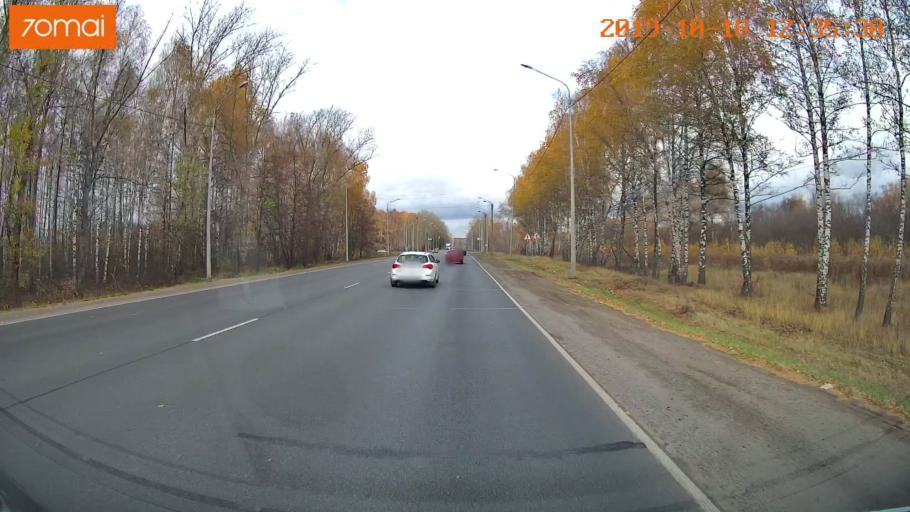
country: RU
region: Rjazan
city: Ryazan'
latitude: 54.6252
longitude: 39.6356
